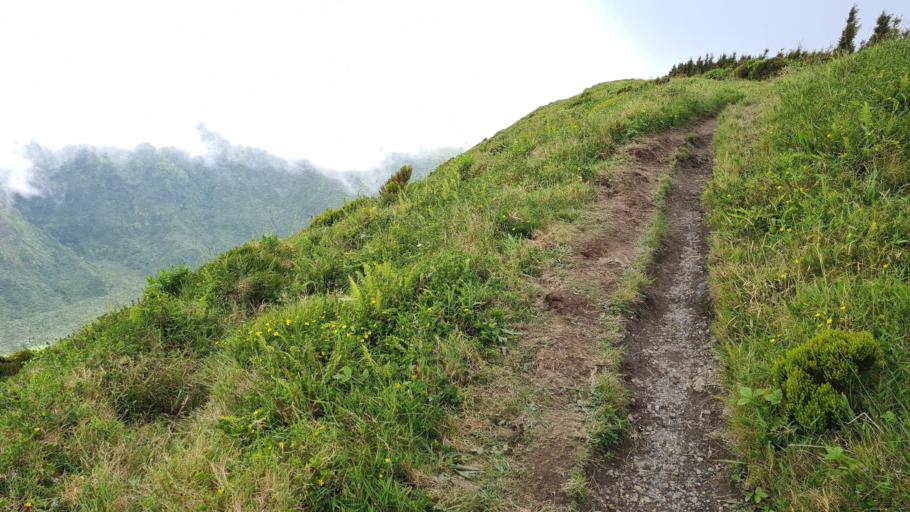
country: PT
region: Azores
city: Ribeira Grande
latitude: 38.5880
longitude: -28.7024
